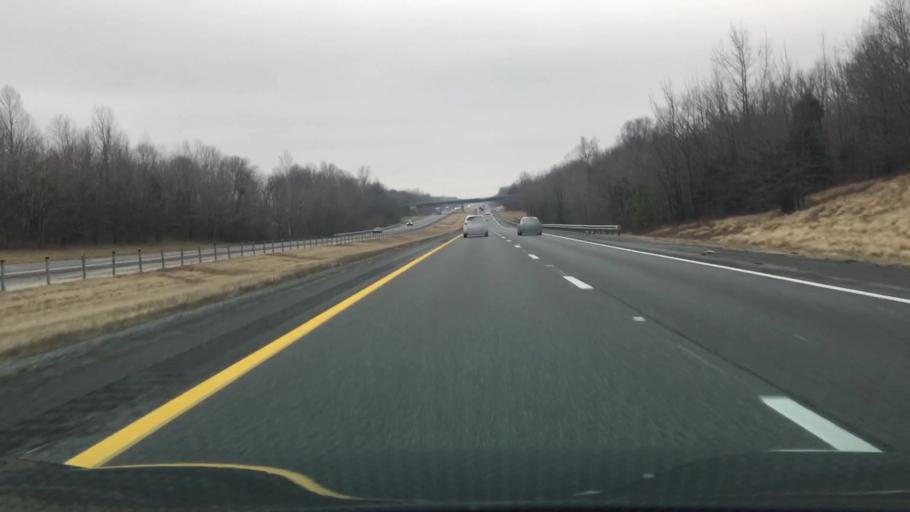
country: US
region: Kentucky
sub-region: McCracken County
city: Reidland
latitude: 36.9954
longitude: -88.5365
